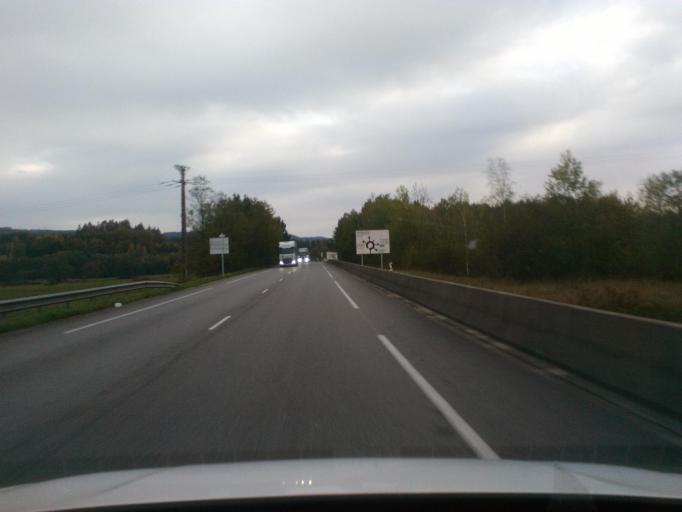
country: FR
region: Lorraine
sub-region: Departement des Vosges
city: Ban-de-Laveline
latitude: 48.2905
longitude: 7.0709
